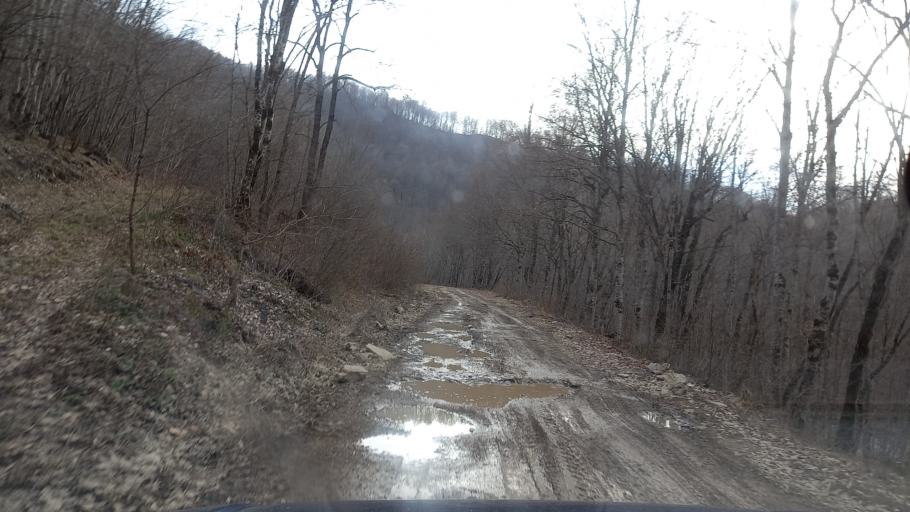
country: RU
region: Adygeya
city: Kamennomostskiy
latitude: 44.1571
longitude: 40.3016
